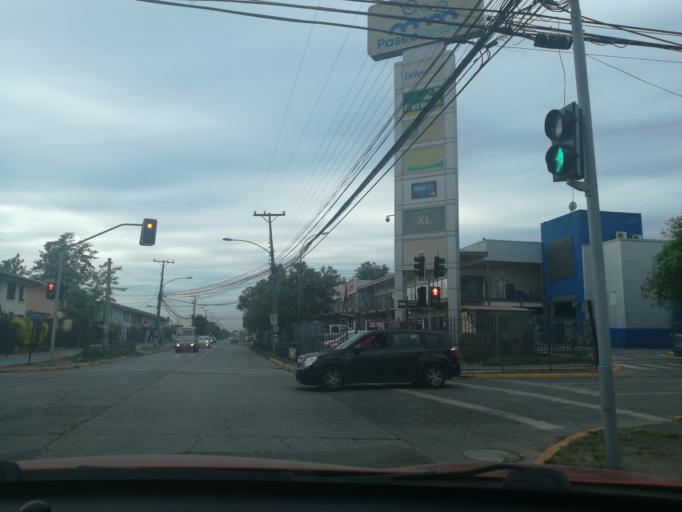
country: CL
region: O'Higgins
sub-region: Provincia de Cachapoal
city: Rancagua
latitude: -34.1598
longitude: -70.7386
